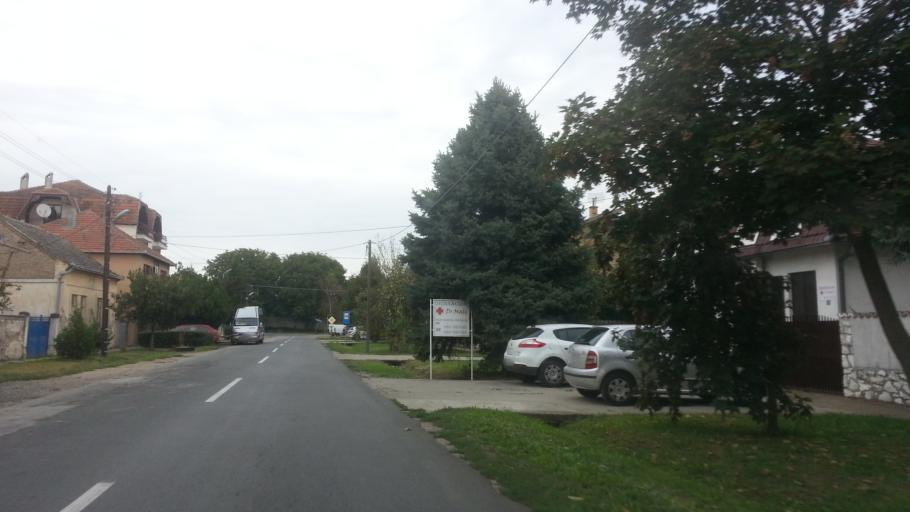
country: RS
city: Stari Banovci
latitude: 44.9892
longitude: 20.2894
